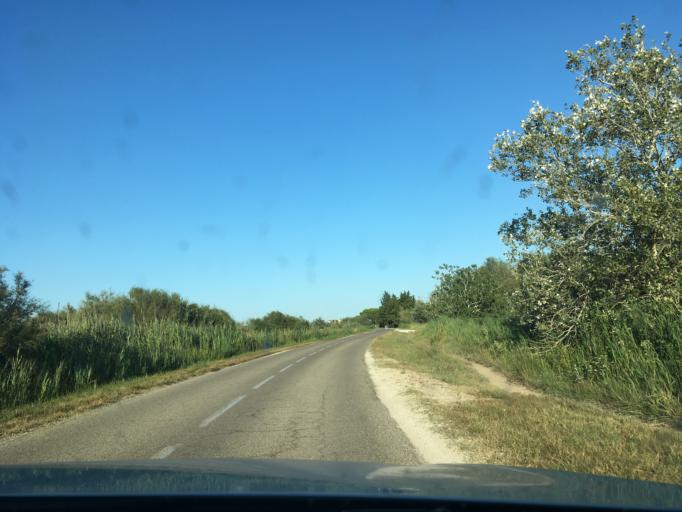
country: FR
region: Provence-Alpes-Cote d'Azur
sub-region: Departement des Bouches-du-Rhone
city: Saintes-Maries-de-la-Mer
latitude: 43.4820
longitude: 4.3993
